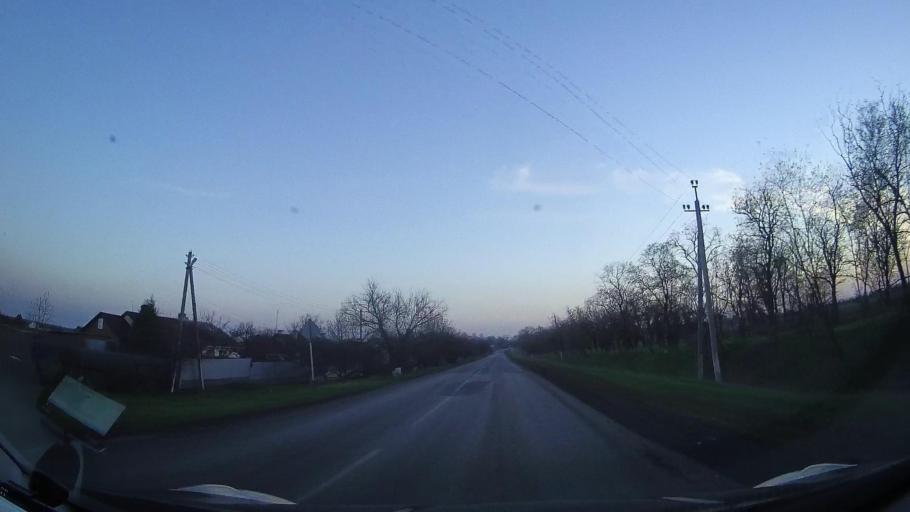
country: RU
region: Rostov
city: Zernograd
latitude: 46.9290
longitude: 40.3663
